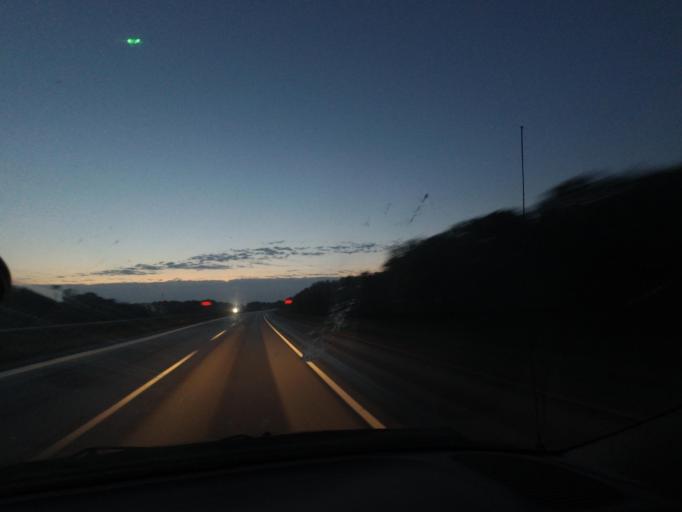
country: US
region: Missouri
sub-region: Linn County
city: Linneus
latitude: 39.7777
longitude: -93.3212
